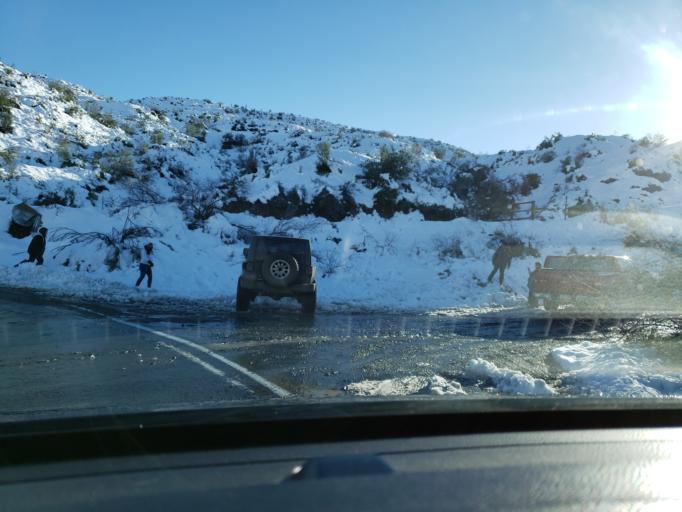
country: US
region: Arizona
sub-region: Maricopa County
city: Carefree
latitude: 33.8968
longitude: -111.8225
